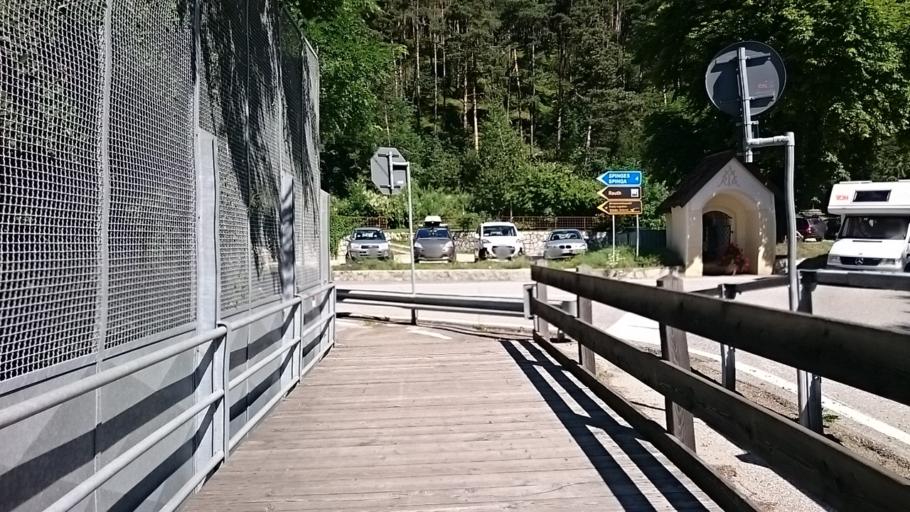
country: IT
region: Trentino-Alto Adige
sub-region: Bolzano
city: Naz-Sciaves - Natz-Schabs
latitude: 46.7747
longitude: 11.6640
